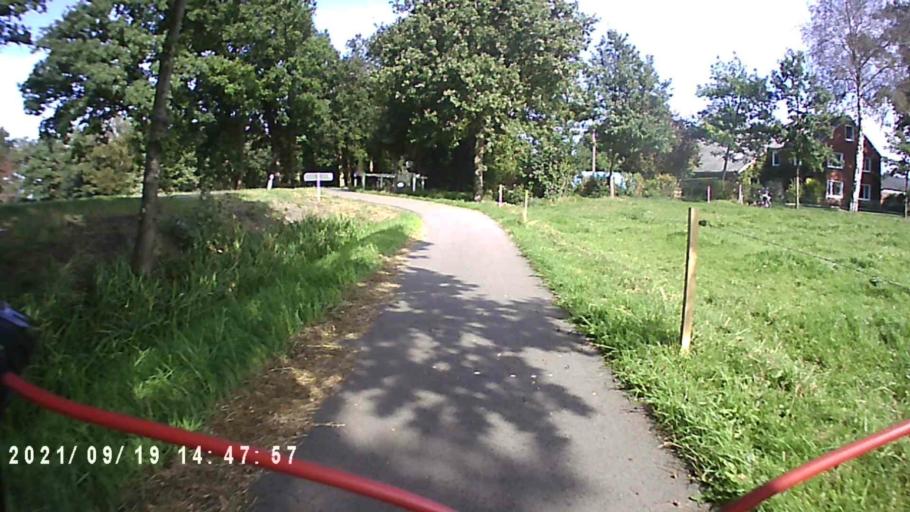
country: DE
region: Lower Saxony
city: Bunde
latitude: 53.1244
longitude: 7.1929
